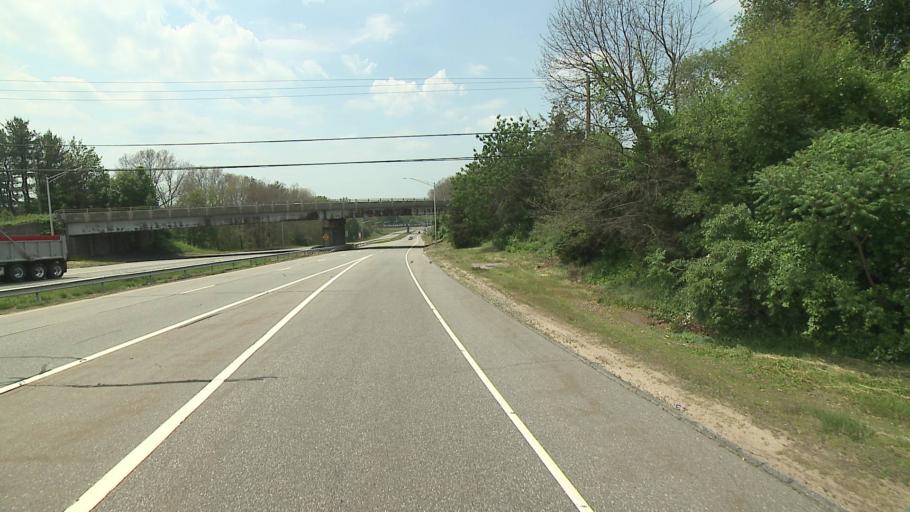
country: US
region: Connecticut
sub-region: Windham County
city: Danielson
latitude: 41.7943
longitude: -71.8792
